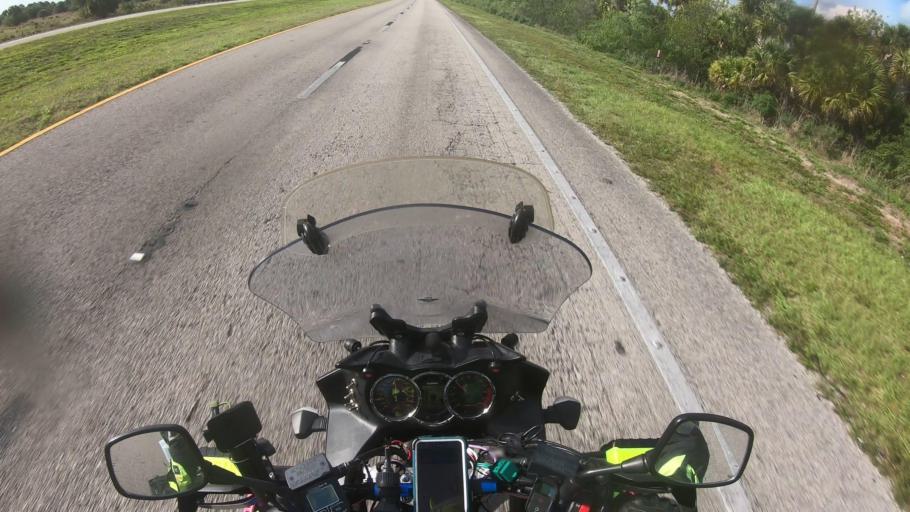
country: US
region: Florida
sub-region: Glades County
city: Moore Haven
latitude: 26.8389
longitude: -81.1941
